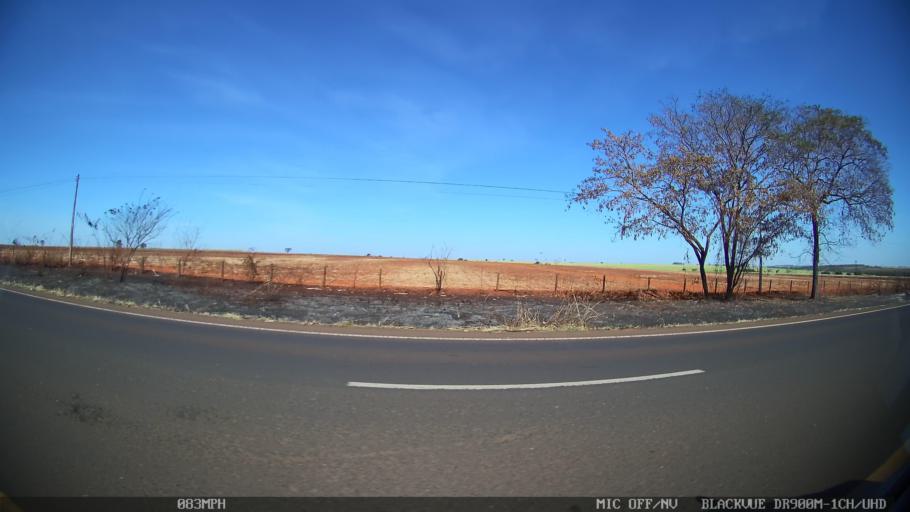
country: BR
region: Sao Paulo
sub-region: Barretos
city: Barretos
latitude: -20.5564
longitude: -48.6442
